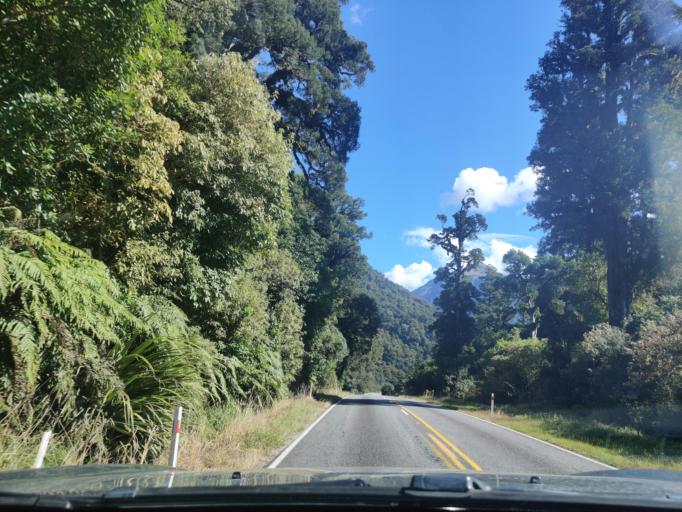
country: NZ
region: Otago
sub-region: Queenstown-Lakes District
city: Wanaka
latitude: -43.9681
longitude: 169.3777
